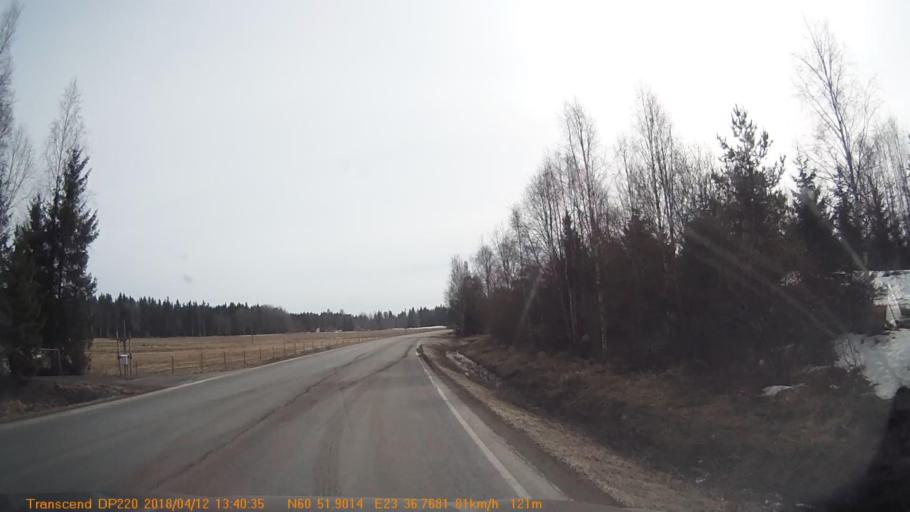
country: FI
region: Haeme
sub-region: Forssa
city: Forssa
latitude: 60.8643
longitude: 23.6133
